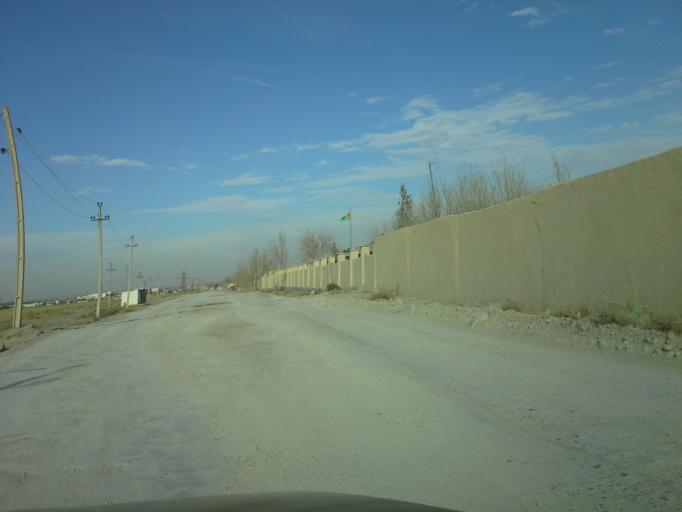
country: TM
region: Ahal
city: Abadan
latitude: 38.0364
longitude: 58.1609
